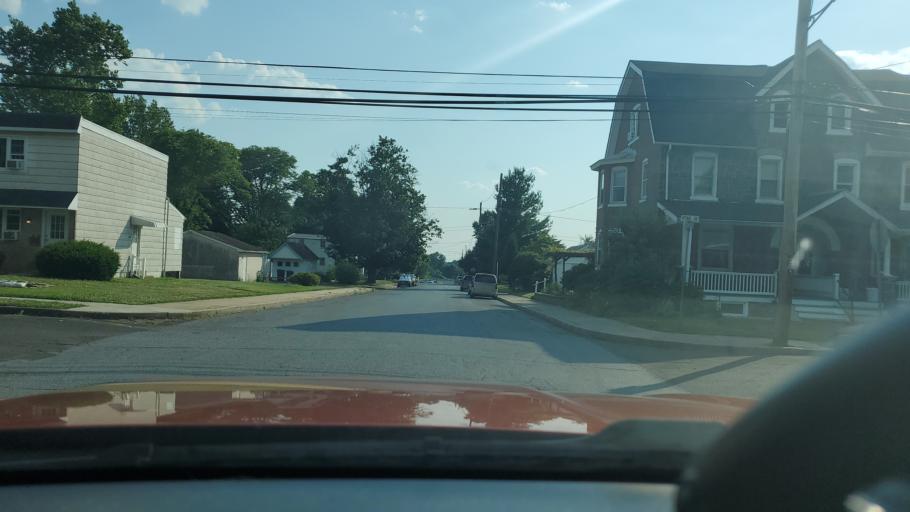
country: US
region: Pennsylvania
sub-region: Montgomery County
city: Souderton
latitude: 40.3052
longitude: -75.3194
